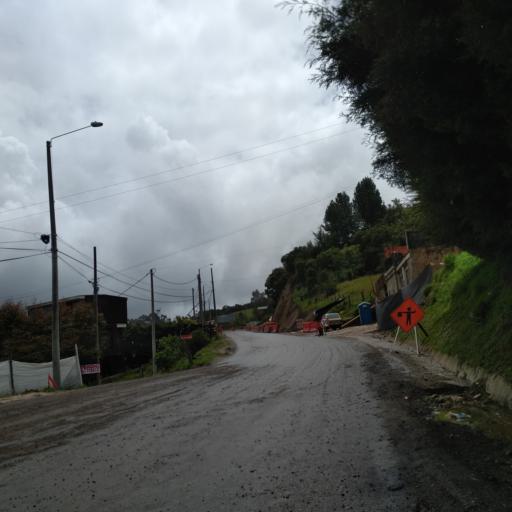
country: CO
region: Bogota D.C.
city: Barrio San Luis
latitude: 4.6792
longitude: -73.9914
